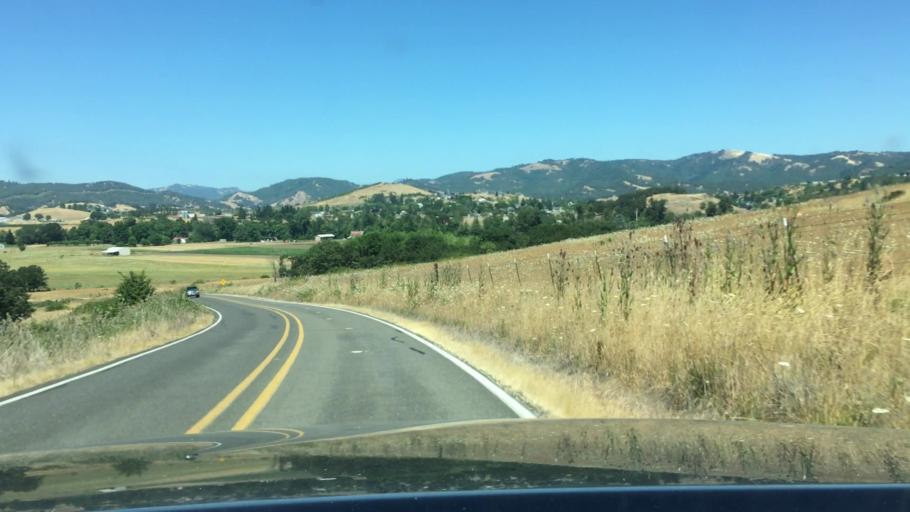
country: US
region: Oregon
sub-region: Douglas County
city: Winston
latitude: 43.1313
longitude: -123.4137
